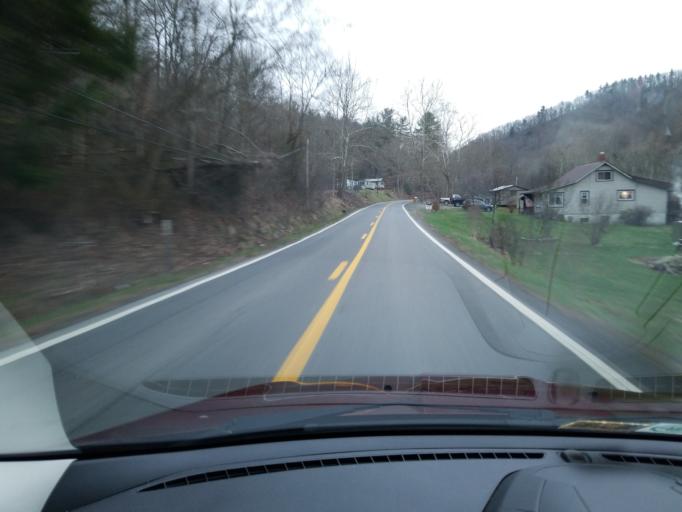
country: US
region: West Virginia
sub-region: Monroe County
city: Union
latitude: 37.5162
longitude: -80.6154
